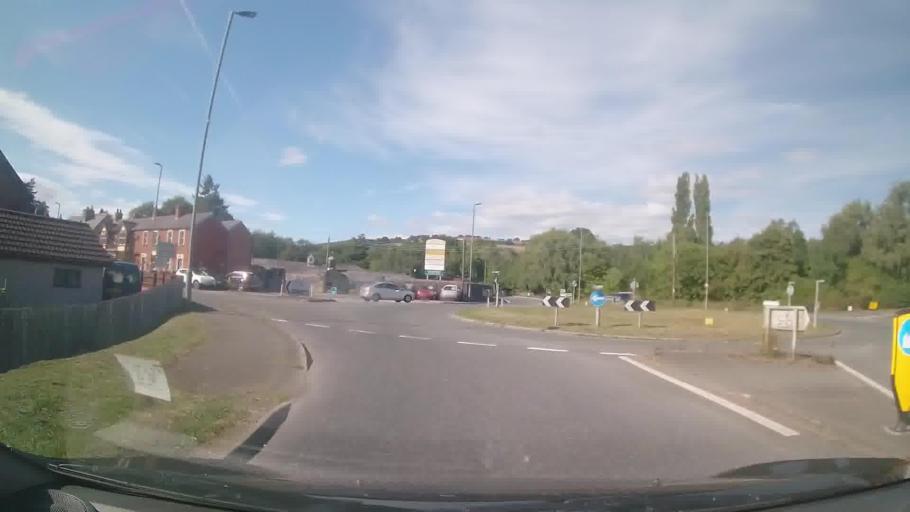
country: GB
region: England
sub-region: Herefordshire
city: Kington
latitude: 52.2059
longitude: -3.0218
